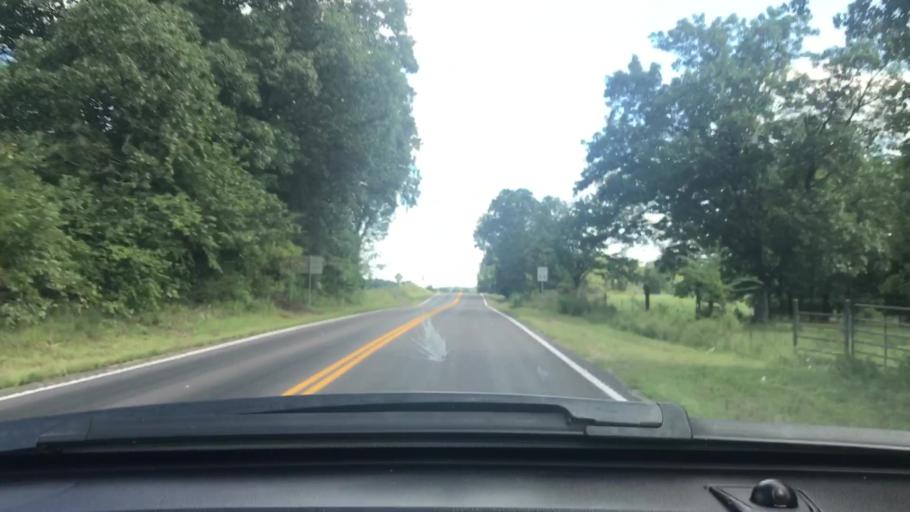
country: US
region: Missouri
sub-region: Wright County
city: Mountain Grove
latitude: 37.2997
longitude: -92.3122
